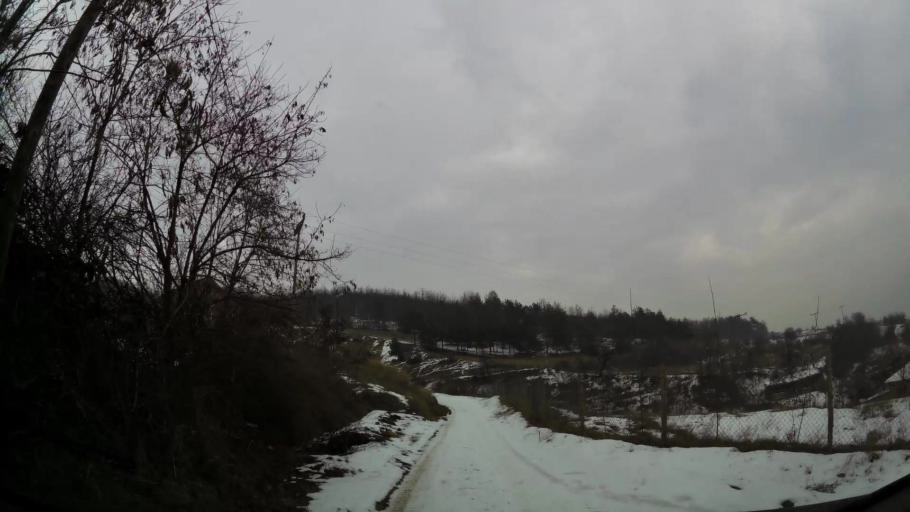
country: MK
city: Kondovo
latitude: 42.0144
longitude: 21.3151
